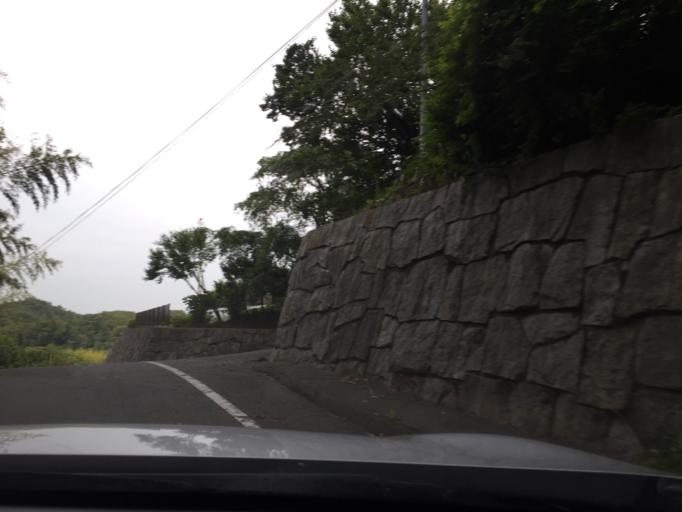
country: JP
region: Fukushima
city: Iwaki
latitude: 37.0466
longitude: 140.9149
